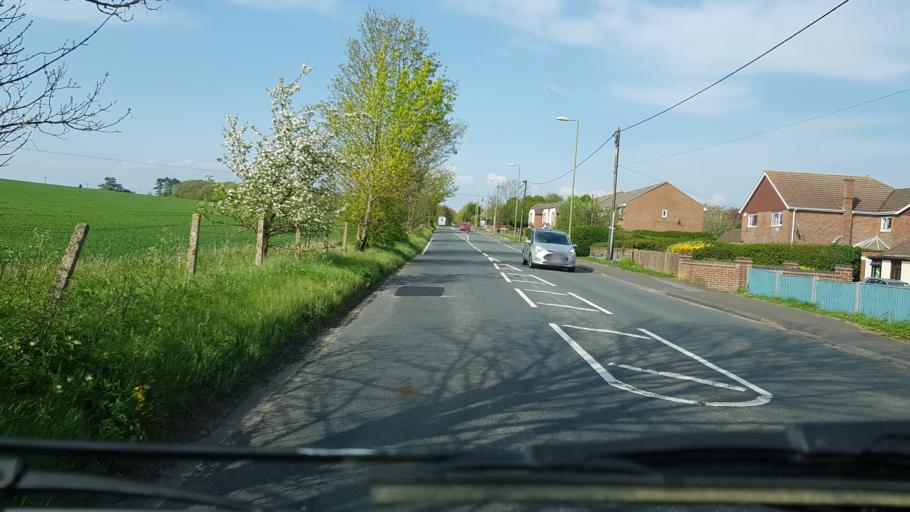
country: GB
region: England
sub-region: Hampshire
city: Basingstoke
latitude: 51.2736
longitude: -1.1281
